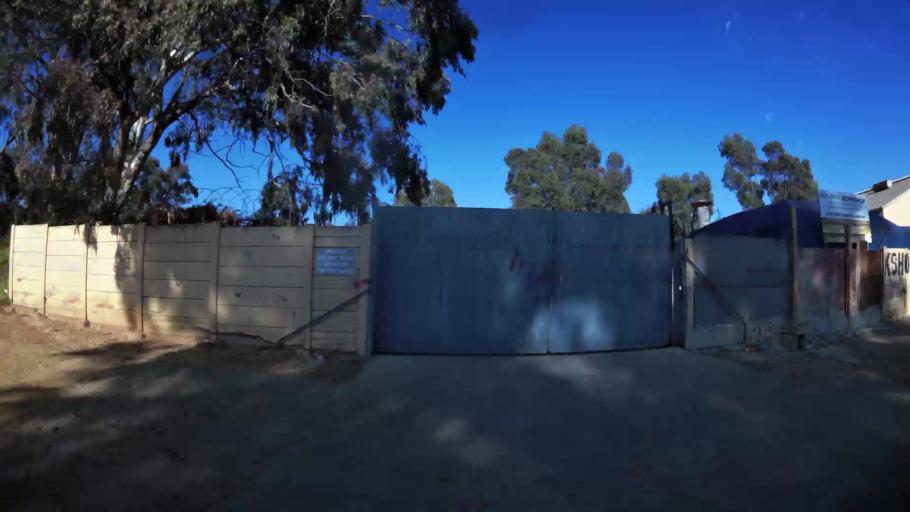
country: ZA
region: Gauteng
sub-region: City of Johannesburg Metropolitan Municipality
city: Roodepoort
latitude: -26.1561
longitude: 27.8566
